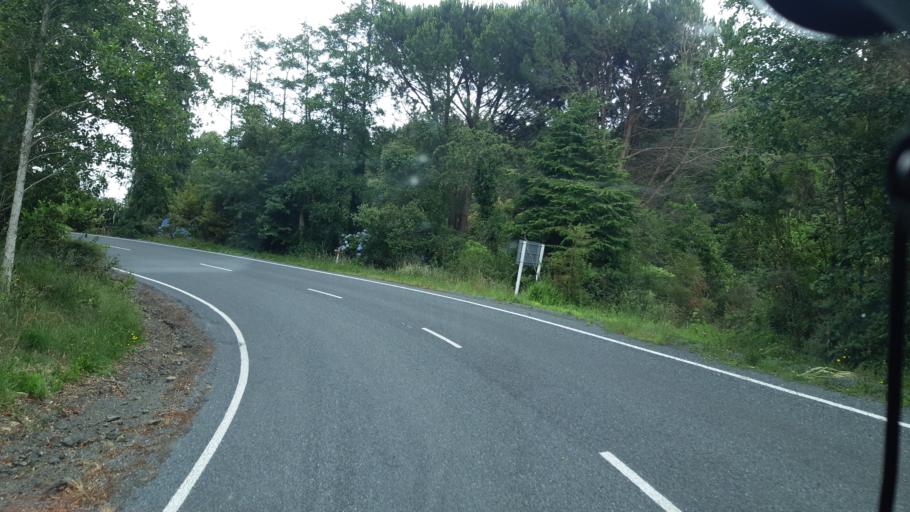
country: NZ
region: Waikato
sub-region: Waikato District
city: Raglan
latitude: -37.8481
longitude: 175.0430
